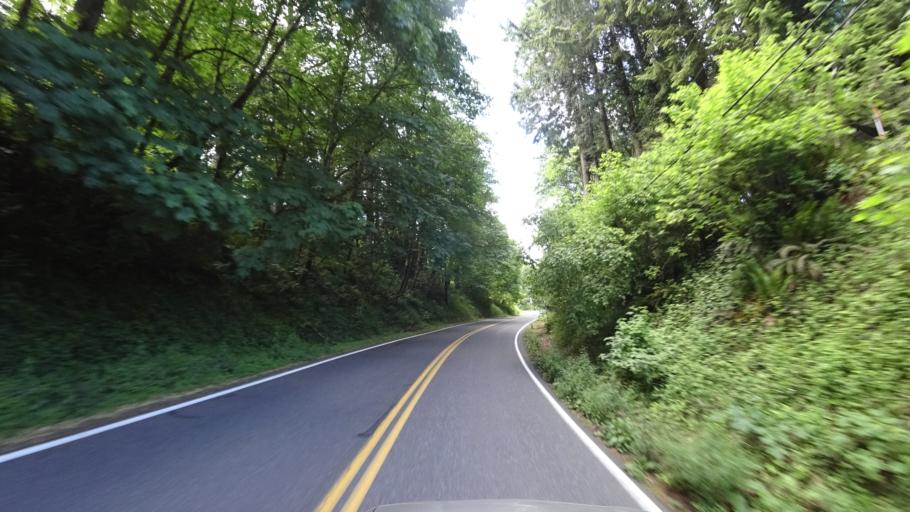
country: US
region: Oregon
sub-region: Washington County
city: Oak Hills
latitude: 45.5904
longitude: -122.8127
